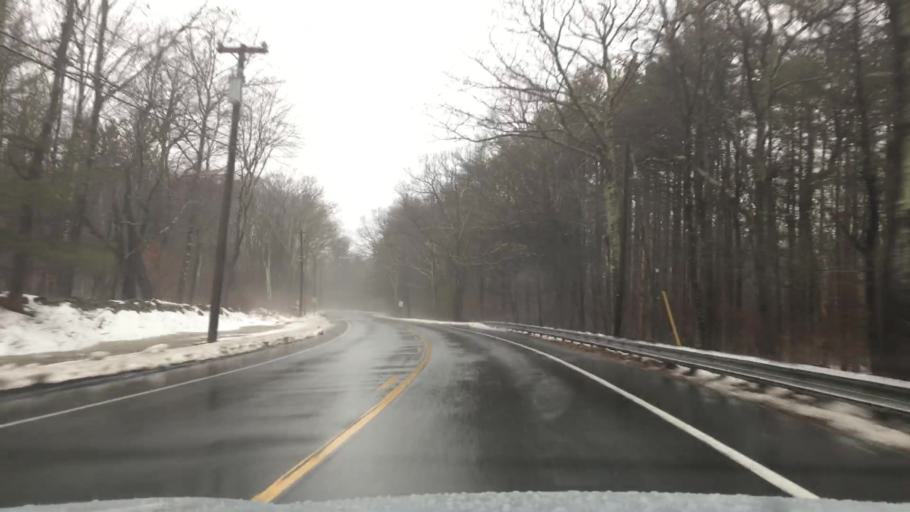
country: US
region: Massachusetts
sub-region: Hampshire County
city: Pelham
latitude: 42.3744
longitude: -72.3999
